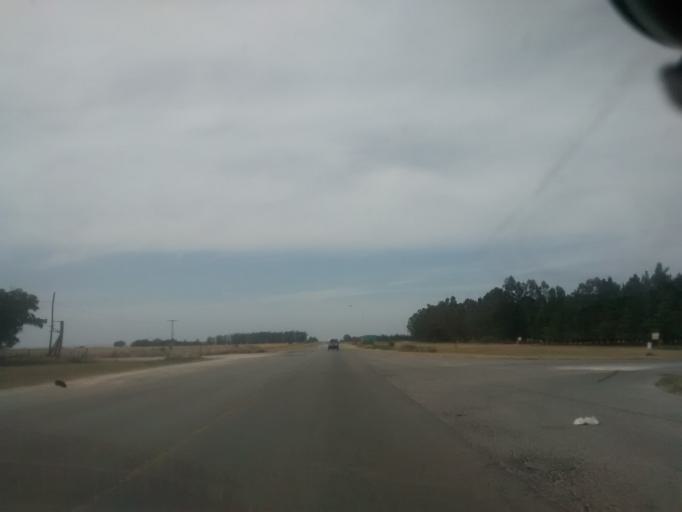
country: AR
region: Buenos Aires
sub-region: Partido de Loberia
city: Loberia
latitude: -38.1397
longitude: -58.7541
